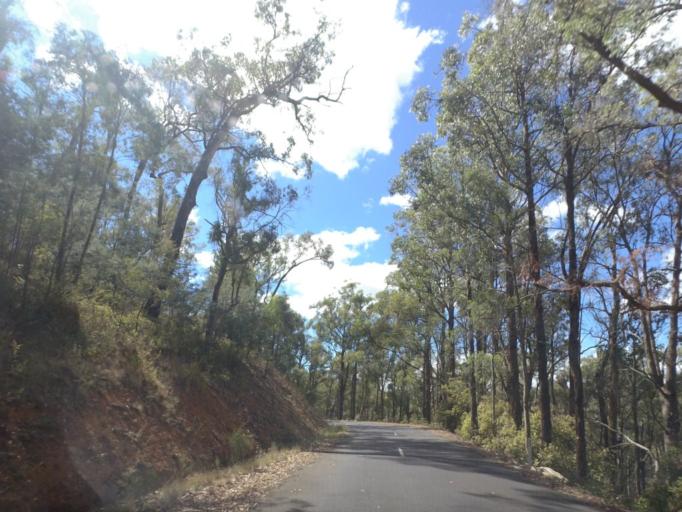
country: AU
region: Victoria
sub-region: Murrindindi
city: Alexandra
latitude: -37.3290
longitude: 145.9432
